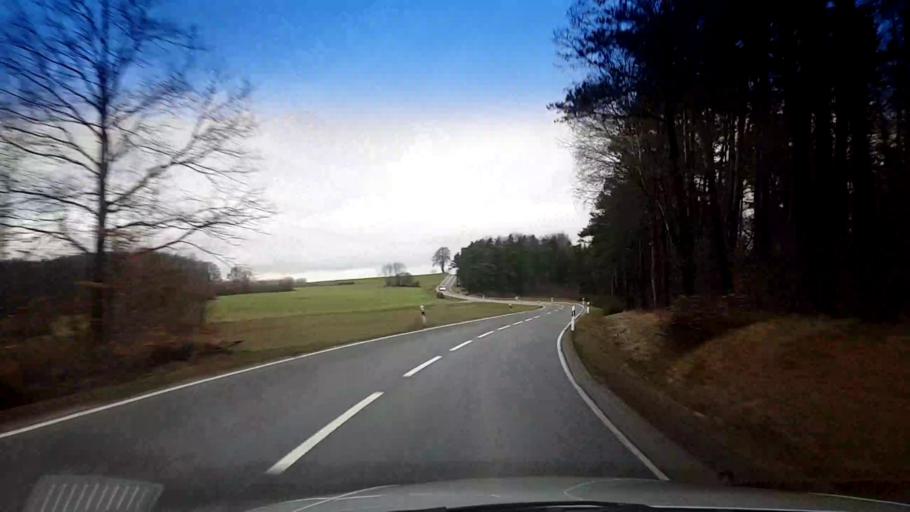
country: DE
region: Bavaria
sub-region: Upper Franconia
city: Wattendorf
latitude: 50.0234
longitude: 11.1244
